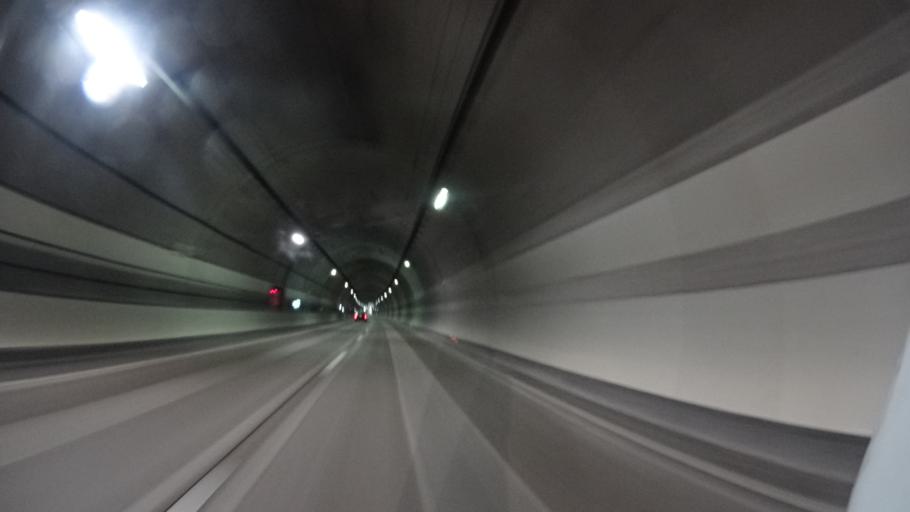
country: JP
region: Kyoto
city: Kyoto
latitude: 34.9723
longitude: 135.7830
